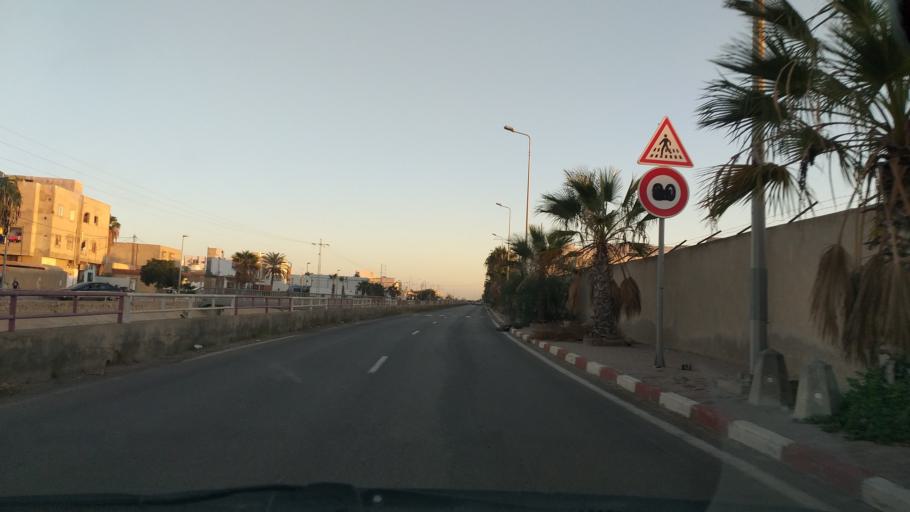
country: TN
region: Safaqis
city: Al Qarmadah
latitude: 34.7656
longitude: 10.7778
